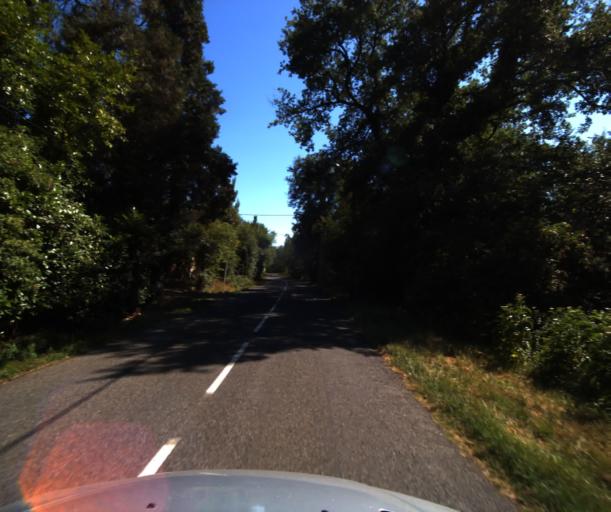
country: FR
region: Midi-Pyrenees
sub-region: Departement de la Haute-Garonne
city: Eaunes
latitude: 43.4386
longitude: 1.3272
